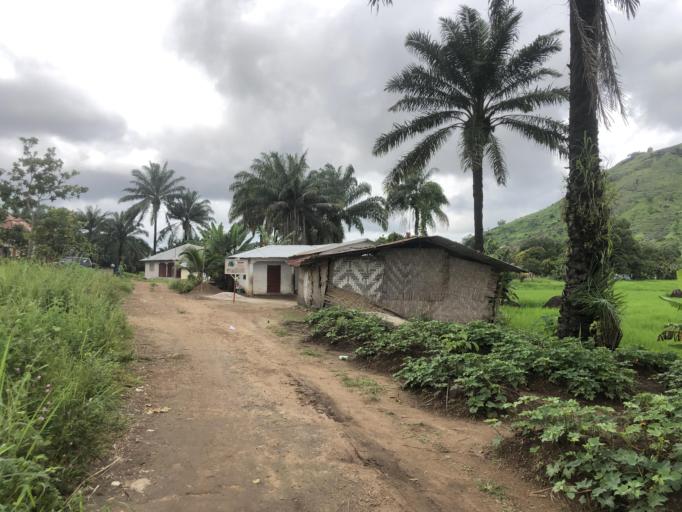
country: SL
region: Northern Province
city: Makeni
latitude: 8.9080
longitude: -12.0422
